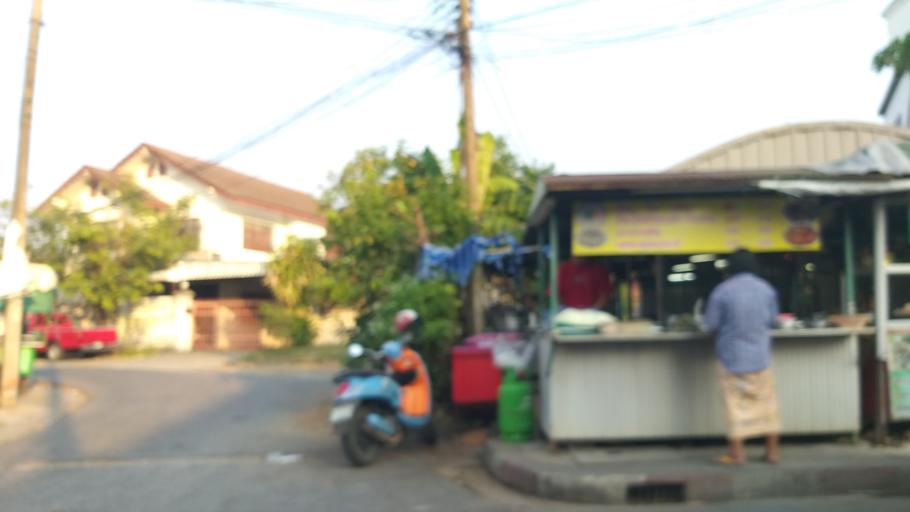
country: TH
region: Khon Kaen
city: Khon Kaen
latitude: 16.4194
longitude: 102.8327
